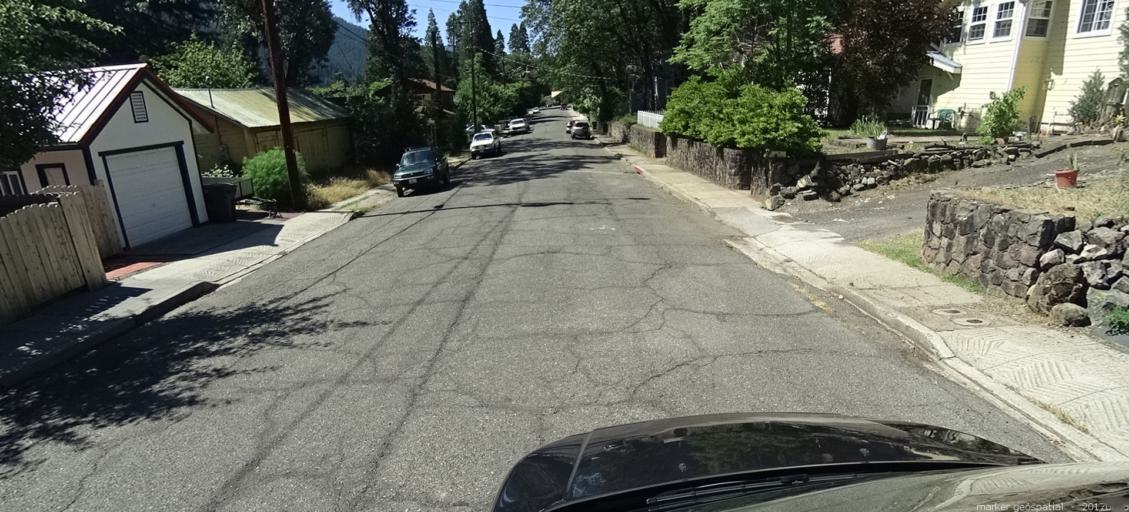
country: US
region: California
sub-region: Siskiyou County
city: Dunsmuir
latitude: 41.2093
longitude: -122.2747
